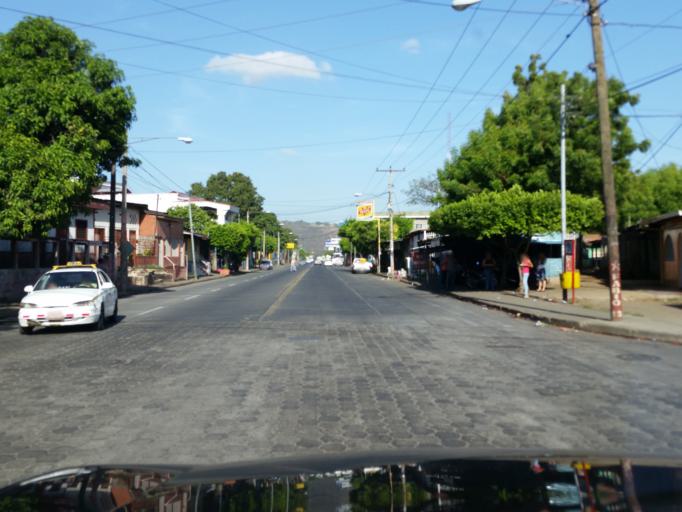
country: NI
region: Managua
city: Ciudad Sandino
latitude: 12.1536
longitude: -86.3007
